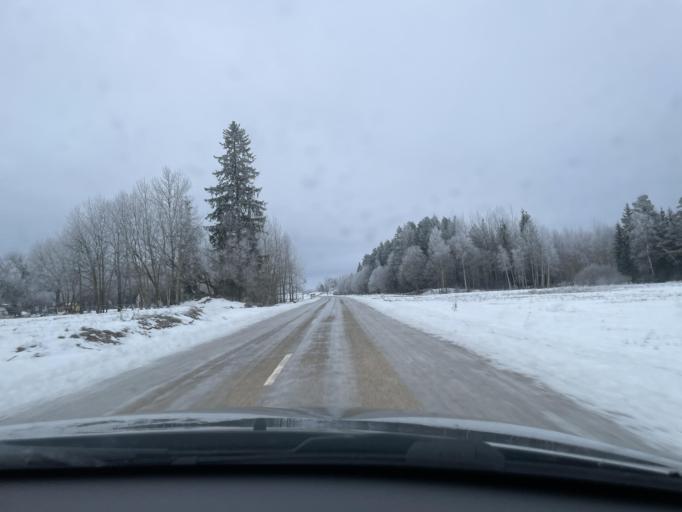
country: LV
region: Ludzas Rajons
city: Ludza
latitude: 56.4478
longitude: 27.5466
